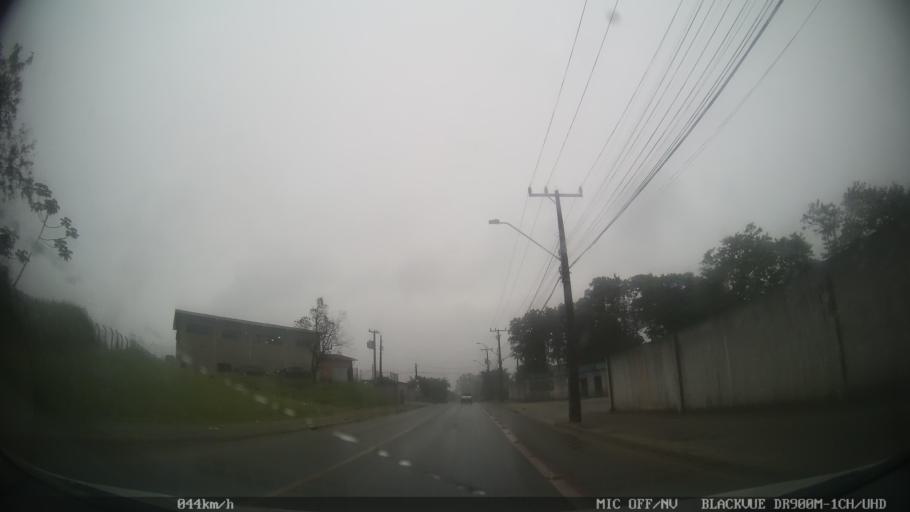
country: BR
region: Santa Catarina
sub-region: Joinville
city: Joinville
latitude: -26.2296
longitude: -48.8184
